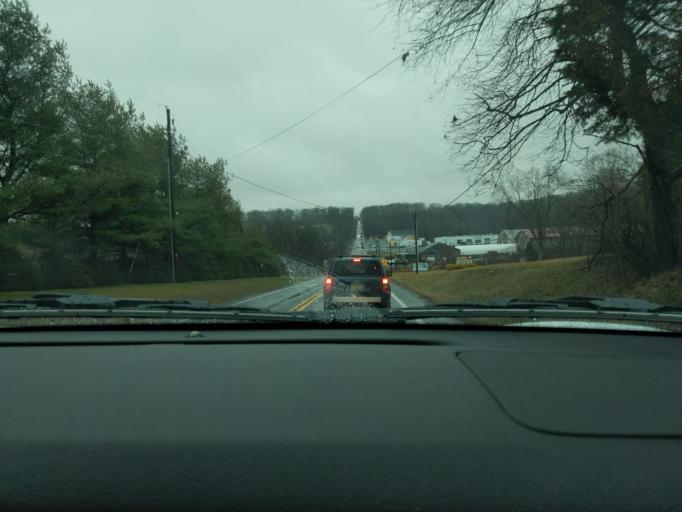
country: US
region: Pennsylvania
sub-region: Bucks County
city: Perkasie
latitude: 40.4013
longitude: -75.2501
